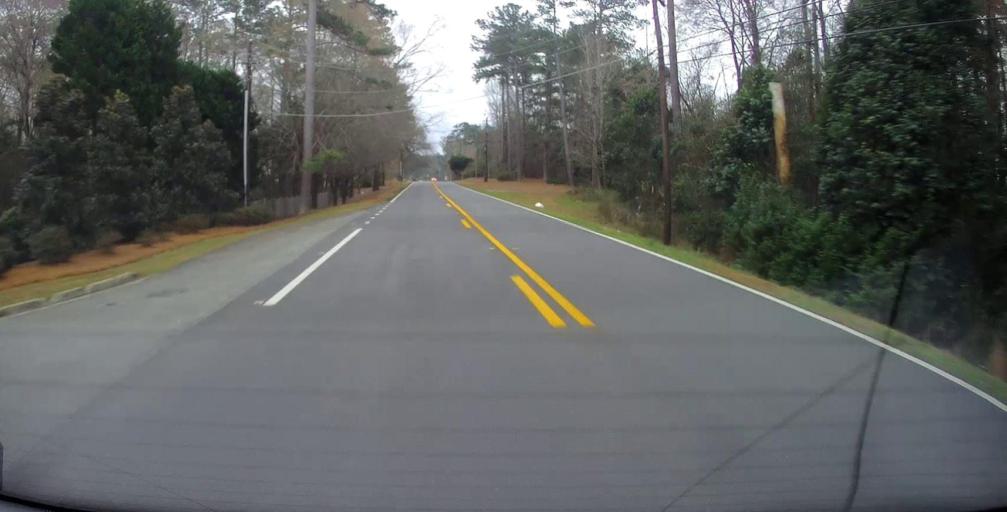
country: US
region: Georgia
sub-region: Bibb County
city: Macon
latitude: 32.9015
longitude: -83.7355
